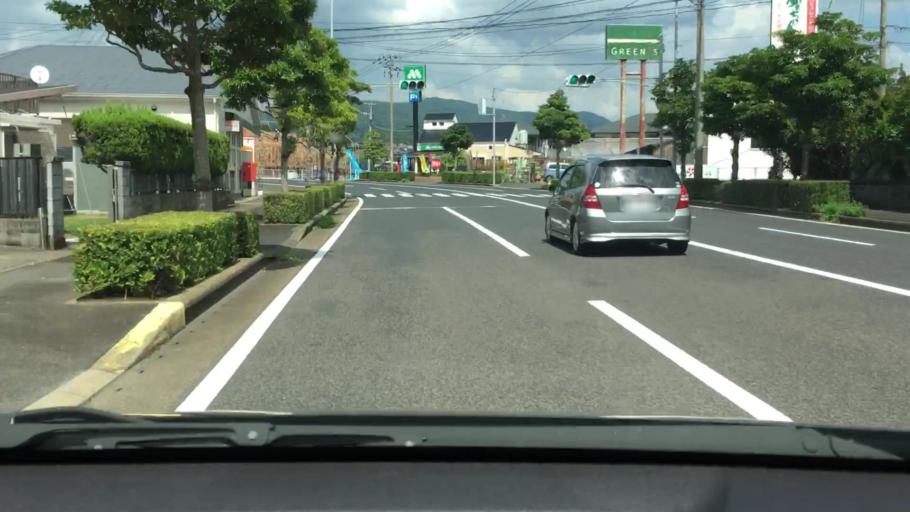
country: JP
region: Nagasaki
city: Sasebo
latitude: 33.2037
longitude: 129.6801
